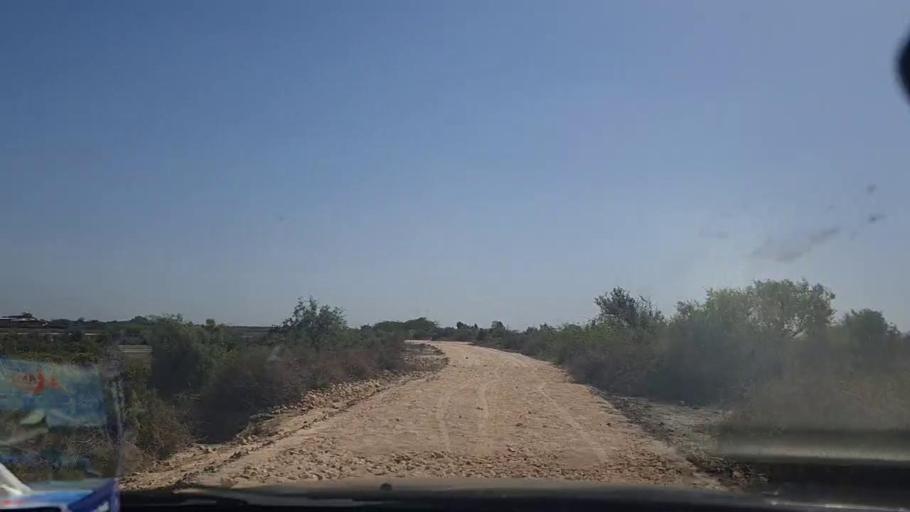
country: PK
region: Sindh
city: Chuhar Jamali
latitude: 24.2711
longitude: 67.7457
